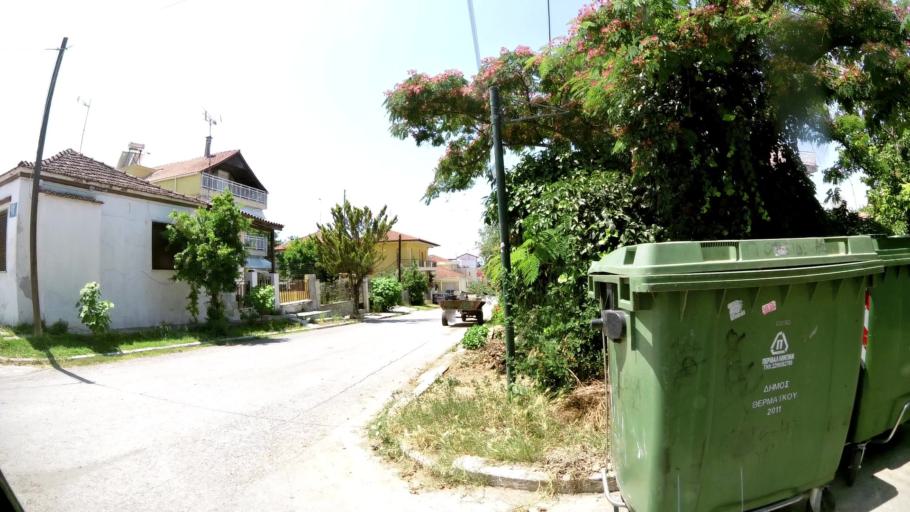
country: GR
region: Central Macedonia
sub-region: Nomos Thessalonikis
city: Nea Michaniona
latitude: 40.4767
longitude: 22.8695
